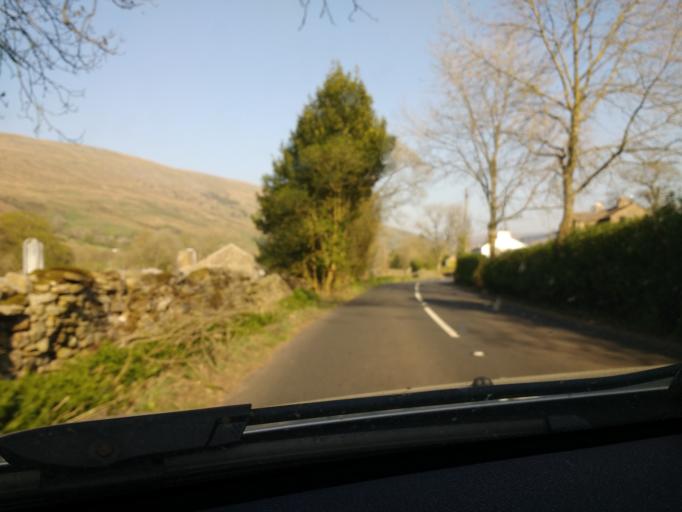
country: GB
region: England
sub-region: Cumbria
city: Sedbergh
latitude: 54.3114
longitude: -2.4496
